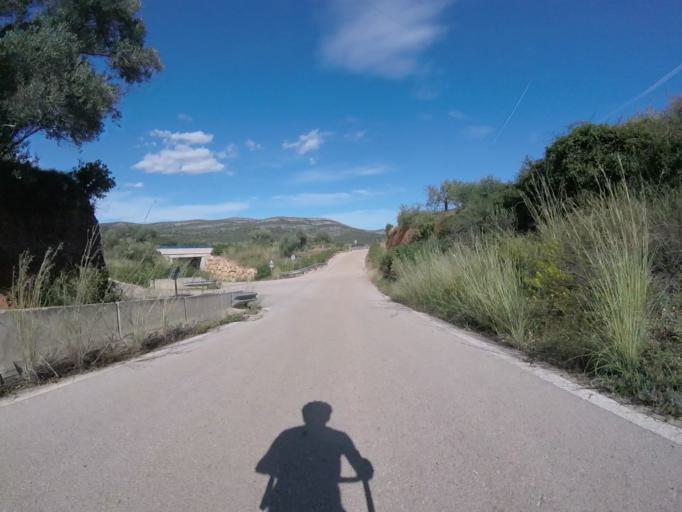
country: ES
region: Valencia
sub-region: Provincia de Castello
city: Santa Magdalena de Pulpis
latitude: 40.3723
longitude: 0.3274
